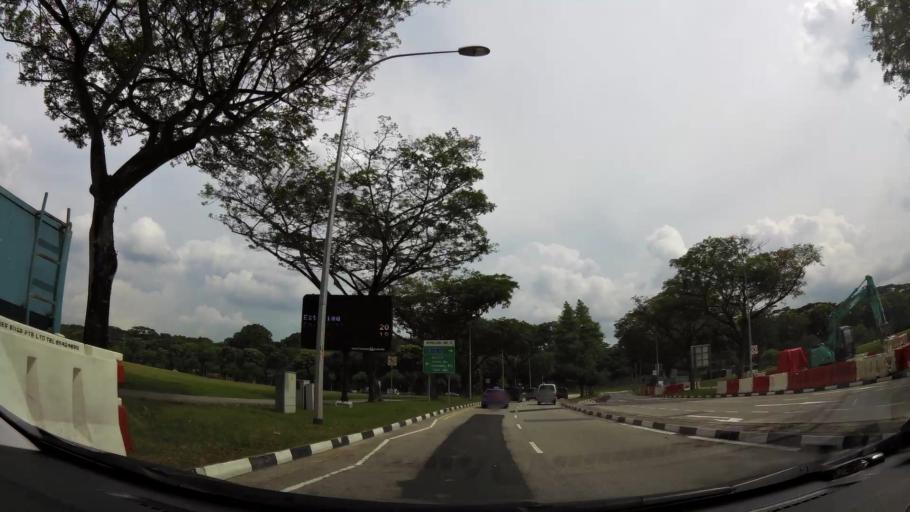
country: MY
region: Johor
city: Johor Bahru
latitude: 1.4277
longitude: 103.7979
